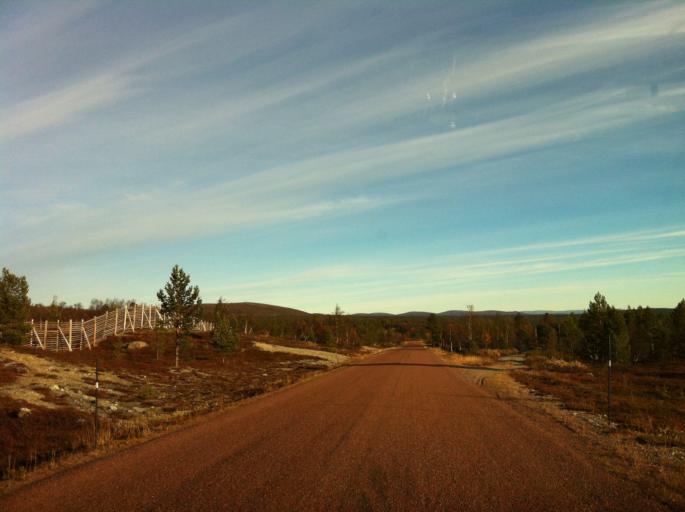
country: NO
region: Hedmark
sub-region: Engerdal
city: Engerdal
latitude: 62.0833
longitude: 12.1015
